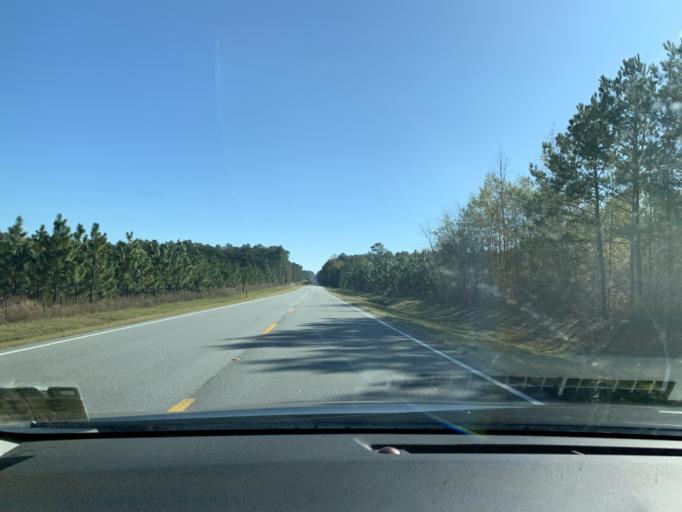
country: US
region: Georgia
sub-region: Ben Hill County
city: Fitzgerald
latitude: 31.7762
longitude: -83.0677
